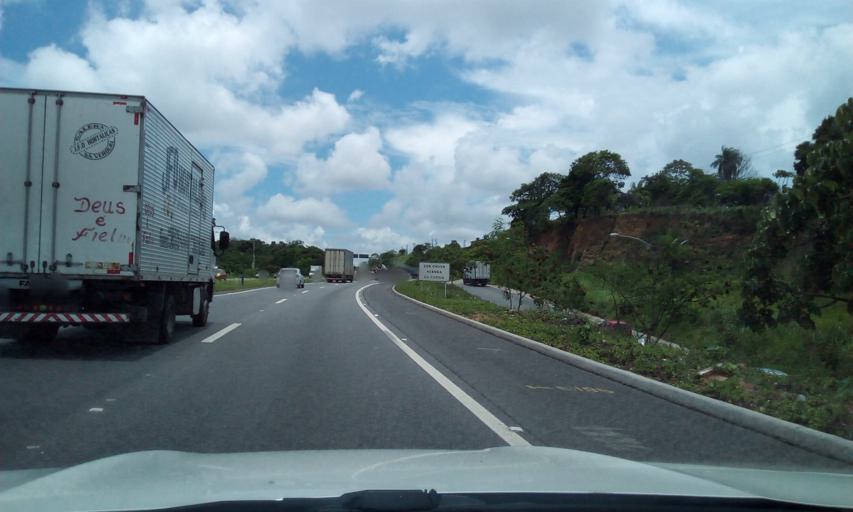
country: BR
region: Pernambuco
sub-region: Paulista
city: Paulista
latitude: -7.9470
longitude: -34.9055
